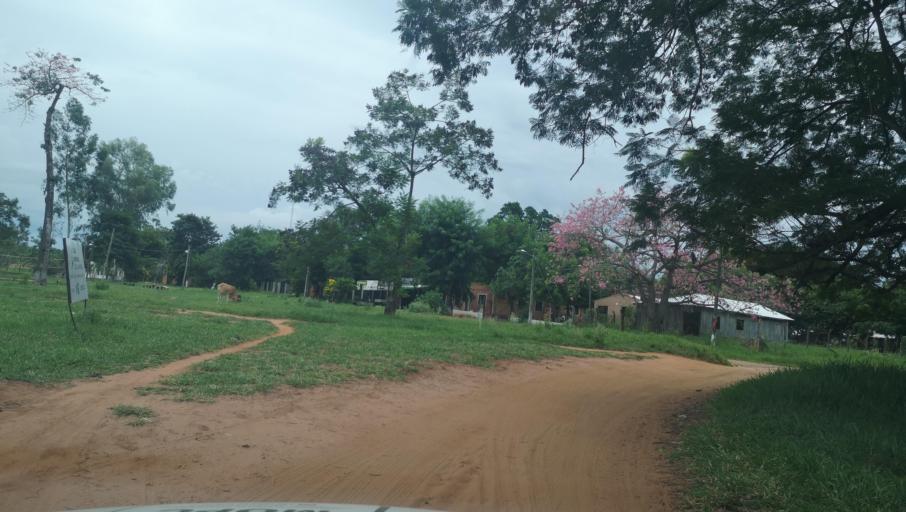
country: PY
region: San Pedro
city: Capiibary
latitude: -24.7262
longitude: -56.0158
